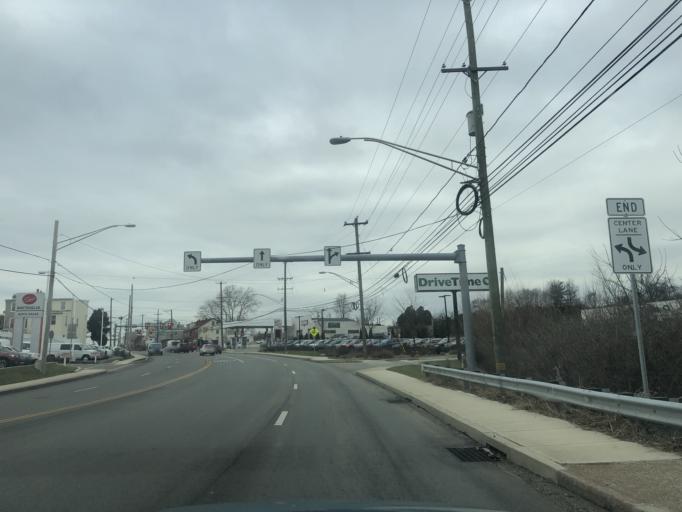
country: US
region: Pennsylvania
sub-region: Montgomery County
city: Norristown
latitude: 40.1074
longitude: -75.3172
